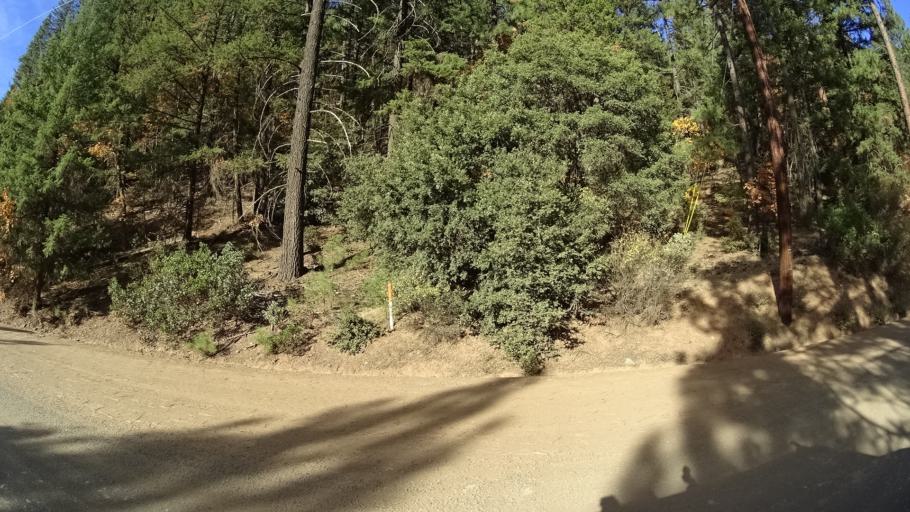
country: US
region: California
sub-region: Siskiyou County
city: Yreka
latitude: 41.6890
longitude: -122.8188
